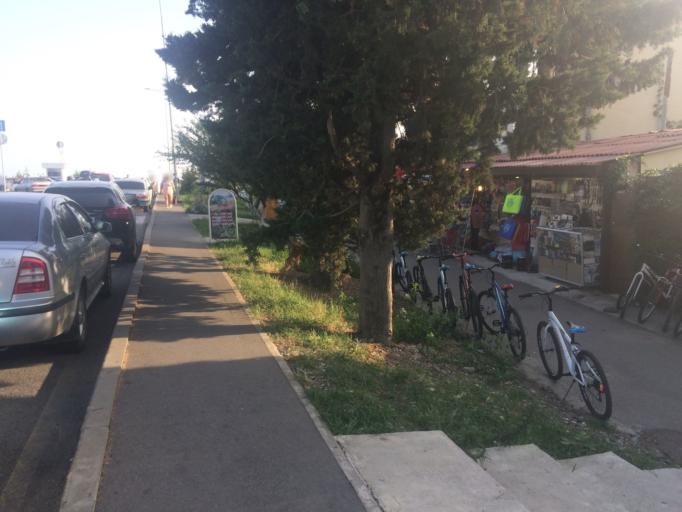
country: RU
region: Krasnodarskiy
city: Adler
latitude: 43.3872
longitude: 39.9908
